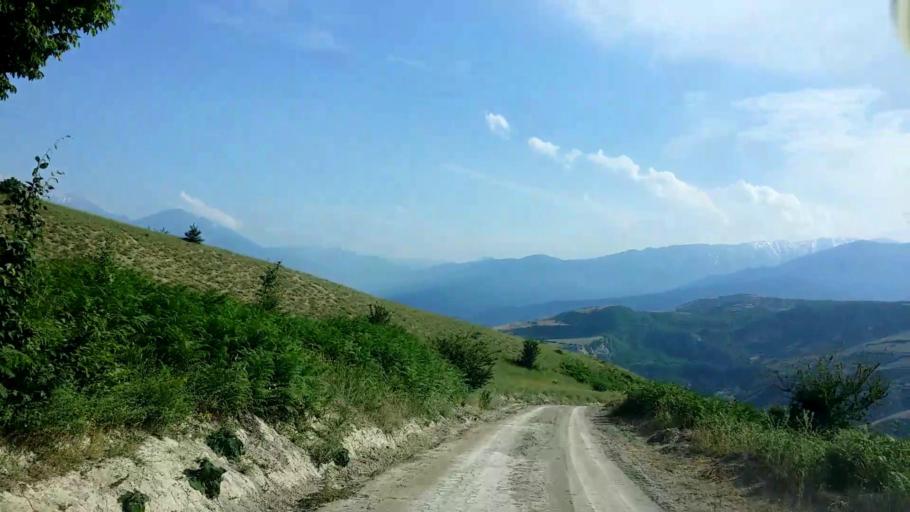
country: IR
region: Mazandaran
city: Chalus
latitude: 36.5502
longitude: 51.2960
